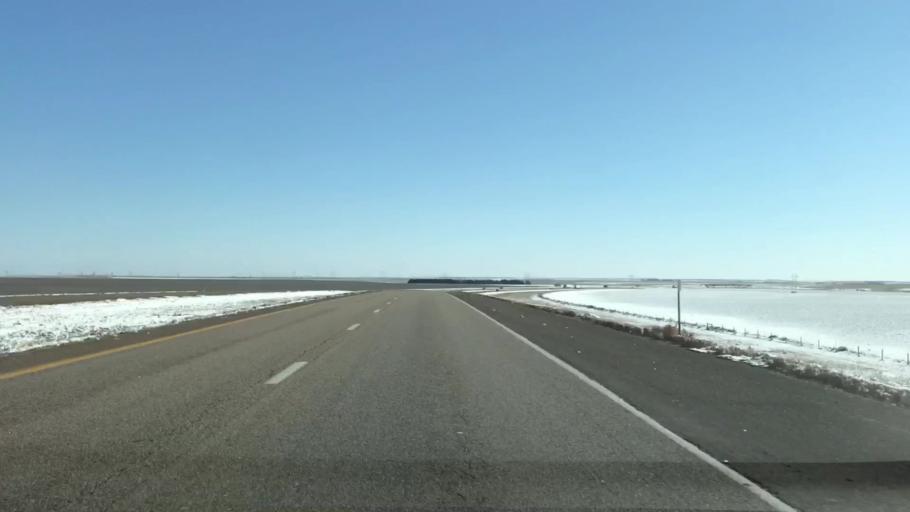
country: US
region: Kansas
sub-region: Thomas County
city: Colby
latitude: 39.3128
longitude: -100.9764
